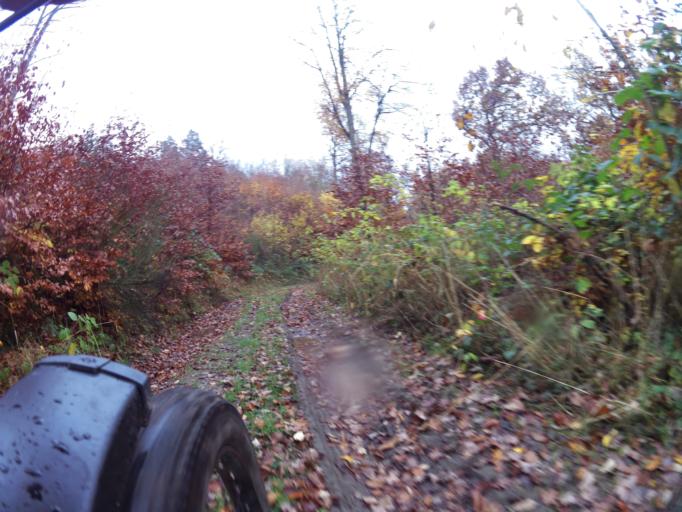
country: PL
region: Pomeranian Voivodeship
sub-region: Powiat wejherowski
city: Gniewino
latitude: 54.7553
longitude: 18.0821
